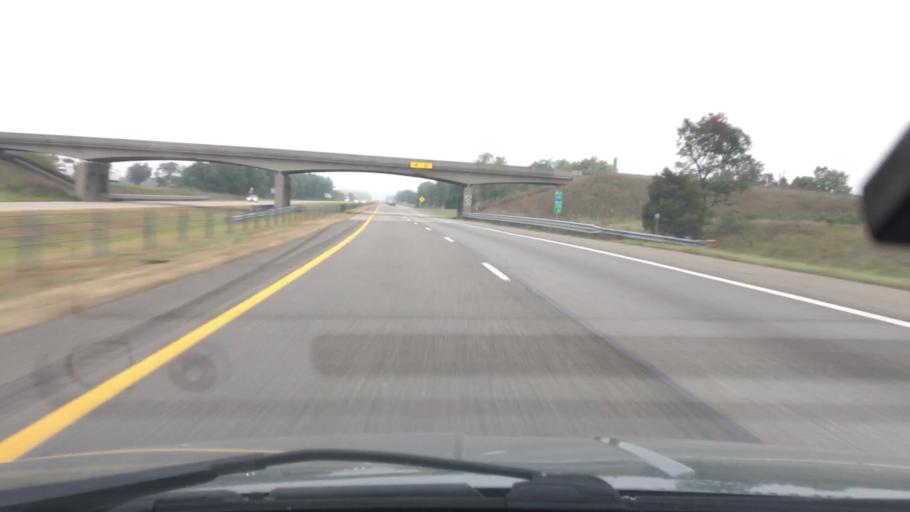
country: US
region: Michigan
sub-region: Calhoun County
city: Albion
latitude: 42.2839
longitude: -84.7998
